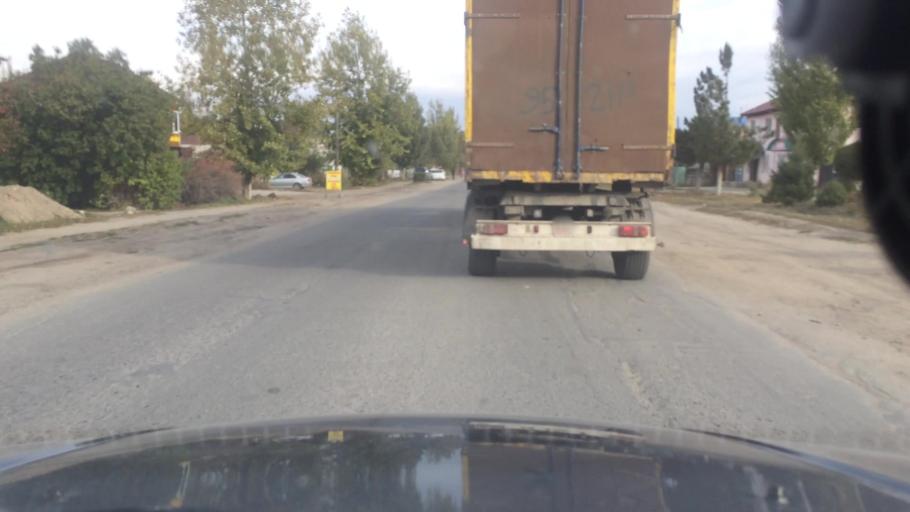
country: KG
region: Ysyk-Koel
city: Karakol
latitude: 42.5189
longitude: 78.3858
